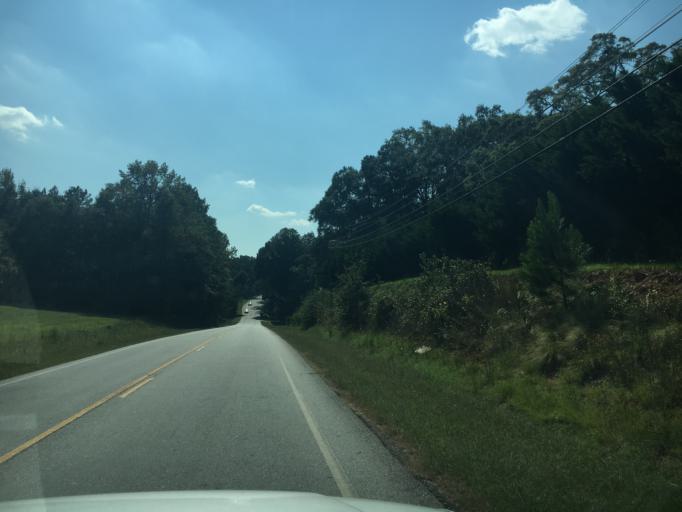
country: US
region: Georgia
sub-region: Franklin County
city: Lavonia
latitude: 34.4471
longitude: -83.1016
